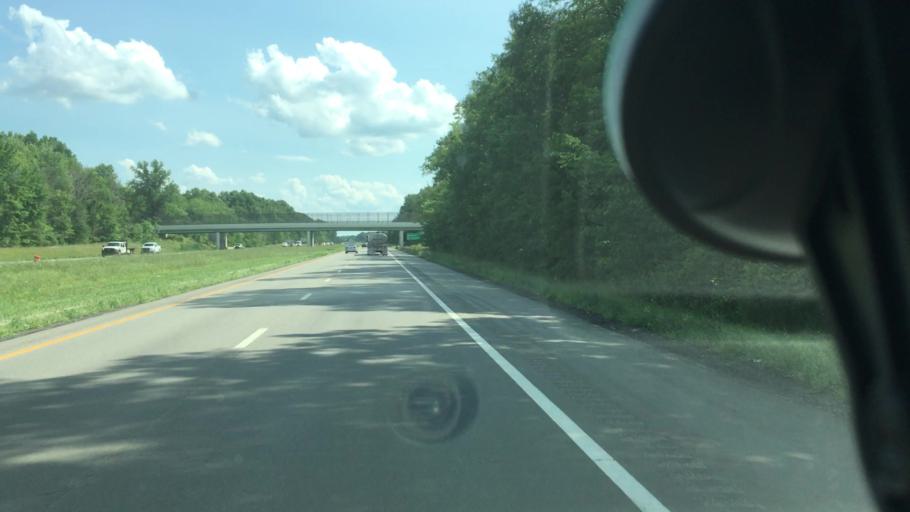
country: US
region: Ohio
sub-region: Mahoning County
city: Austintown
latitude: 41.0860
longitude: -80.7522
